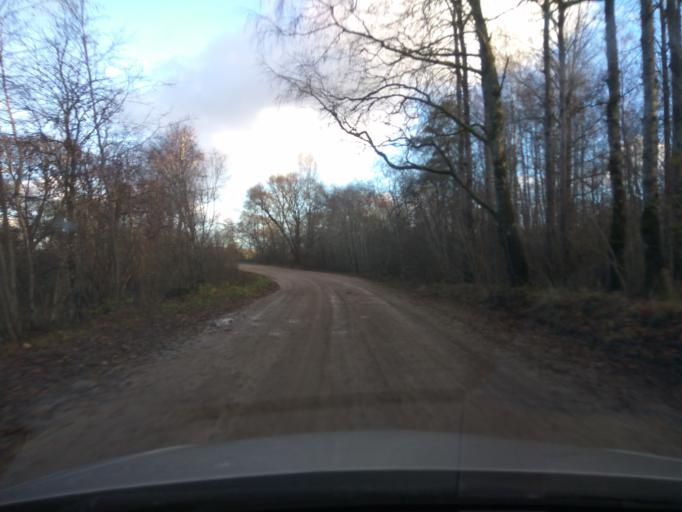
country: LV
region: Aizpute
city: Aizpute
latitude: 56.7479
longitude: 21.6006
